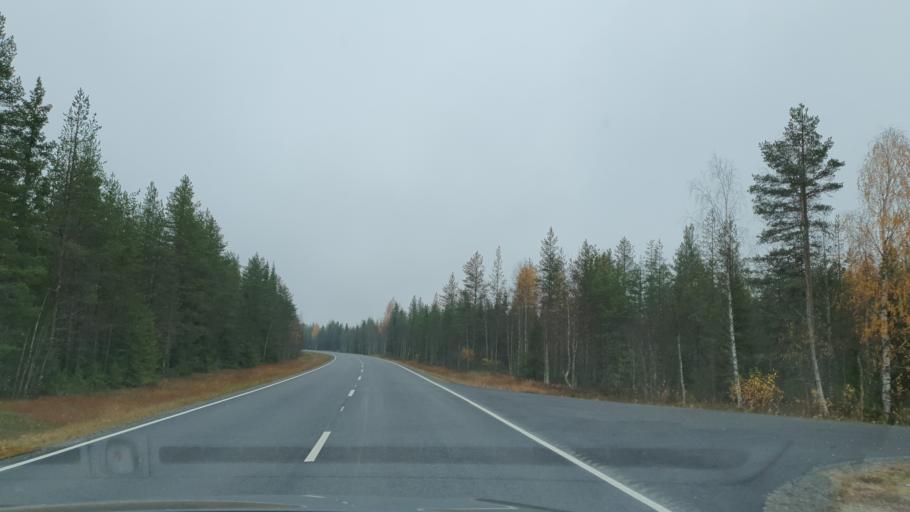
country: FI
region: Lapland
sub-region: Rovaniemi
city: Ranua
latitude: 66.1335
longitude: 26.2787
